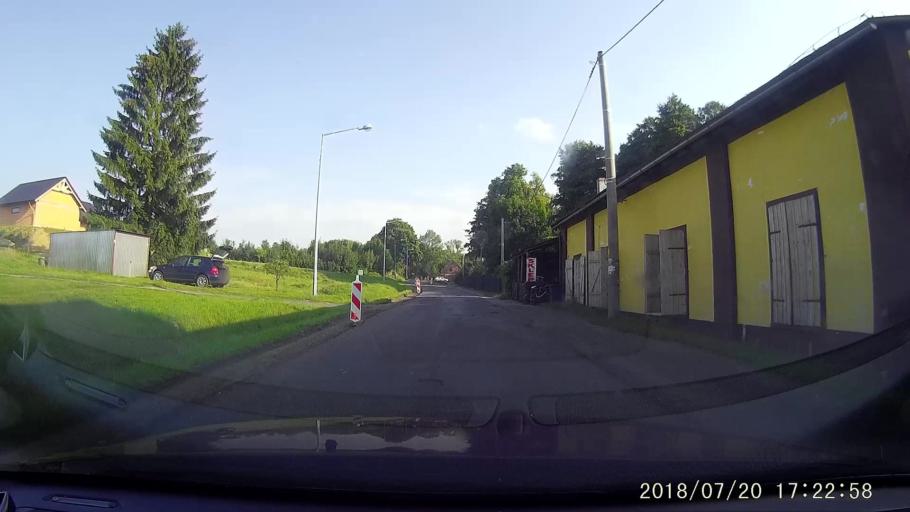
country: PL
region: Lower Silesian Voivodeship
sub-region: Powiat lubanski
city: Lesna
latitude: 50.9756
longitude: 15.2891
